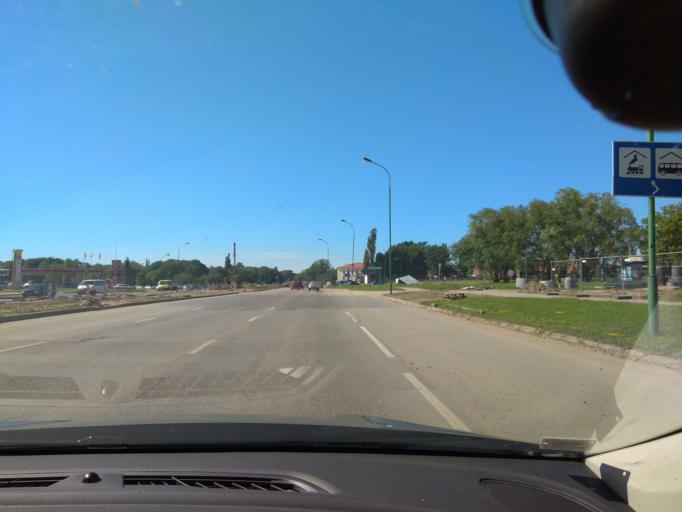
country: LT
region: Klaipedos apskritis
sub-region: Klaipeda
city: Klaipeda
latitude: 55.7037
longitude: 21.1633
